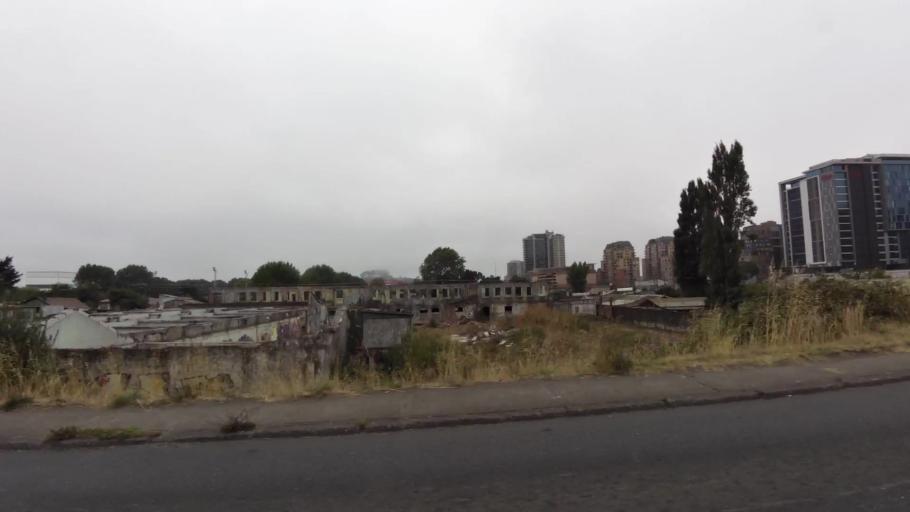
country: CL
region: Biobio
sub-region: Provincia de Concepcion
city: Concepcion
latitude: -36.8359
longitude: -73.0570
